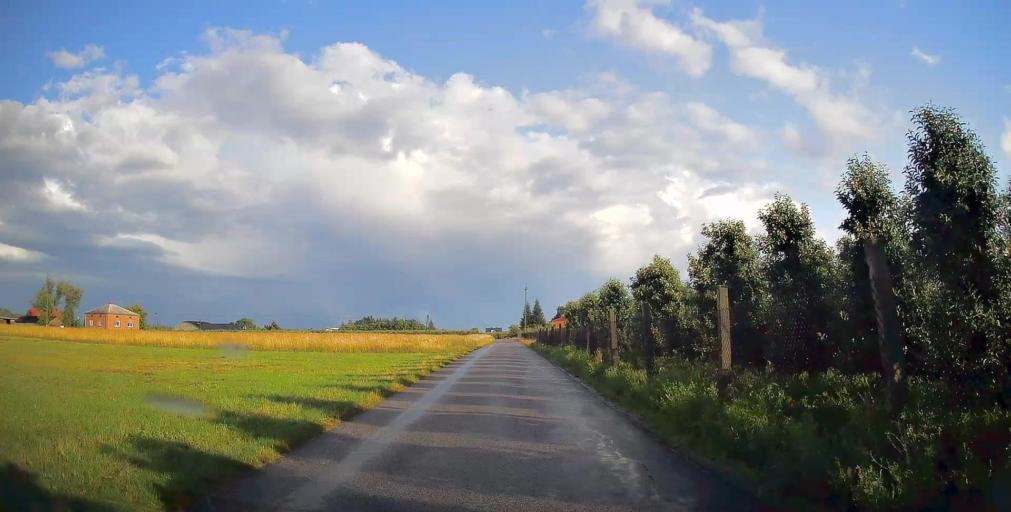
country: PL
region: Masovian Voivodeship
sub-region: Powiat grojecki
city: Goszczyn
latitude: 51.7552
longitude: 20.8819
